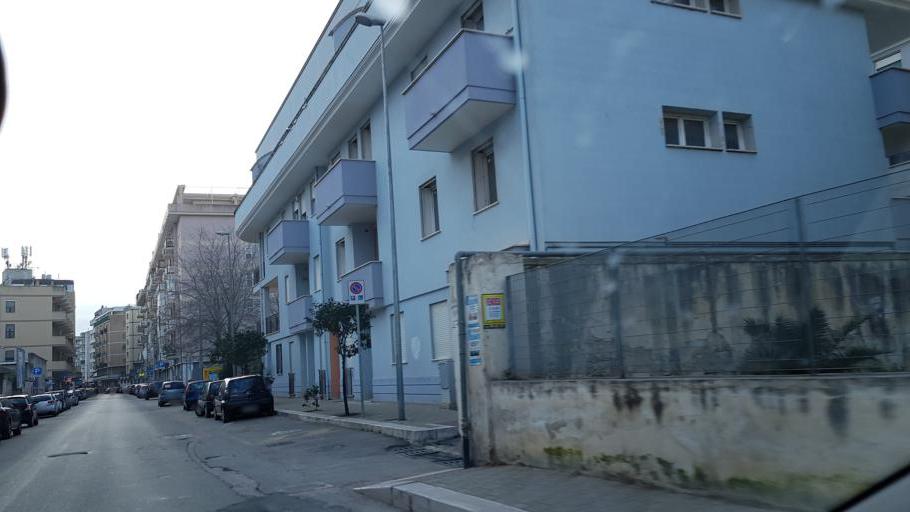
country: IT
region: Apulia
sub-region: Provincia di Brindisi
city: Brindisi
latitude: 40.6363
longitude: 17.9314
